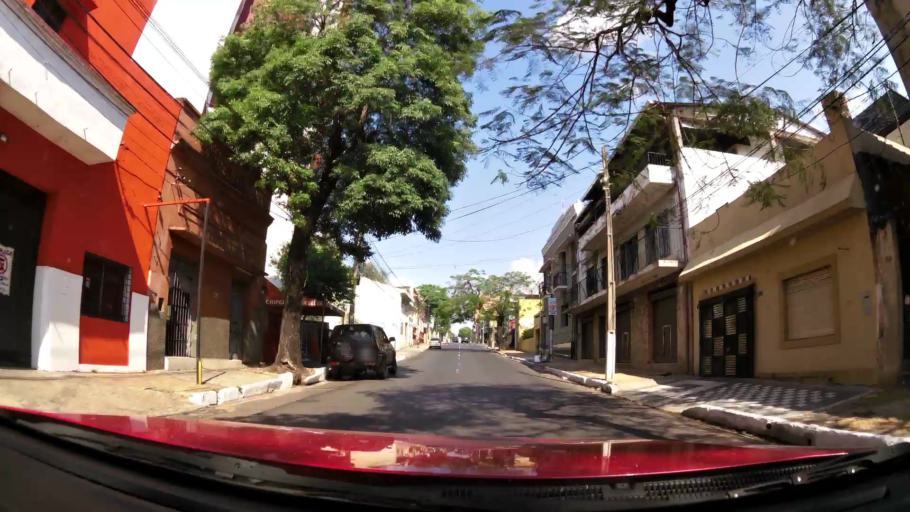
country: PY
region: Asuncion
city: Asuncion
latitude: -25.2855
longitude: -57.6261
